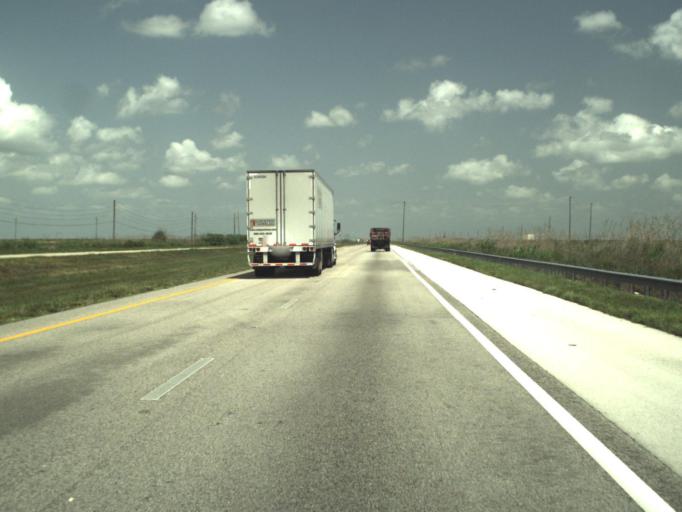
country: US
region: Florida
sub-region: Broward County
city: Coral Springs
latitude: 26.3606
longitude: -80.5575
